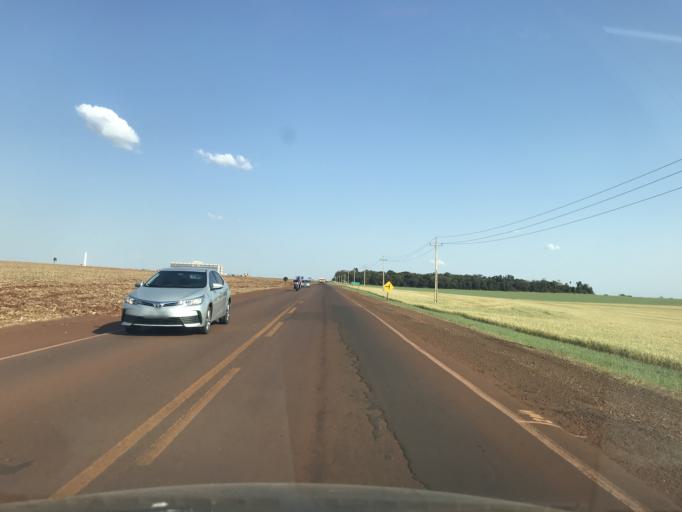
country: BR
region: Parana
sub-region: Toledo
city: Toledo
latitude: -24.6087
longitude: -53.7132
